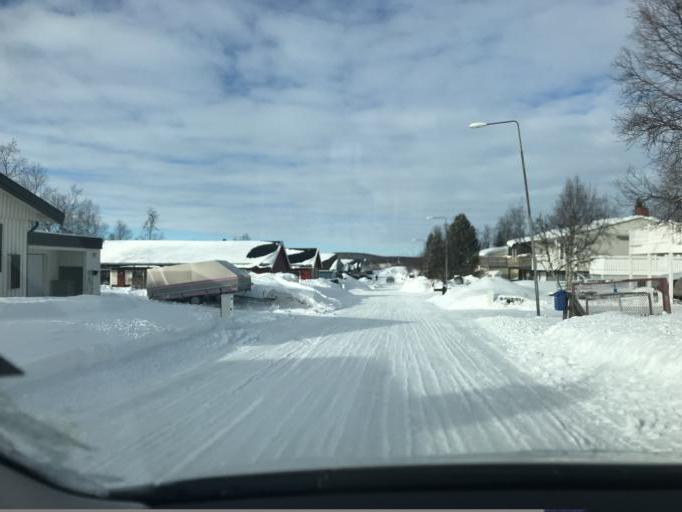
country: SE
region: Norrbotten
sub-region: Kiruna Kommun
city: Kiruna
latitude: 67.8656
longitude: 20.2063
